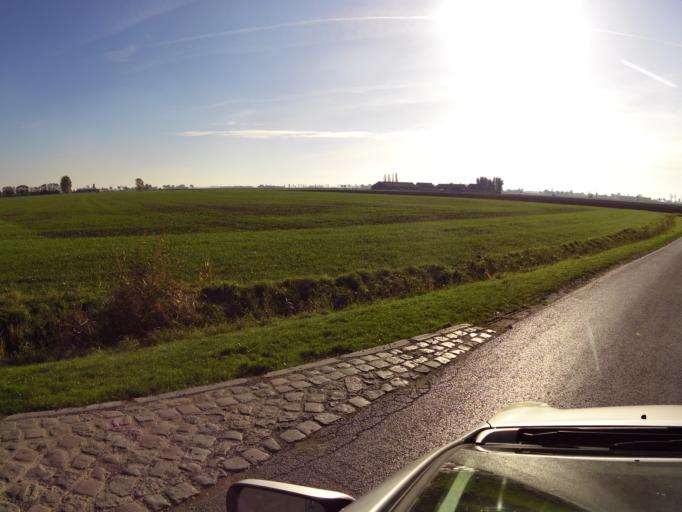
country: BE
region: Flanders
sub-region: Provincie West-Vlaanderen
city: Middelkerke
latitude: 51.1326
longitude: 2.8565
